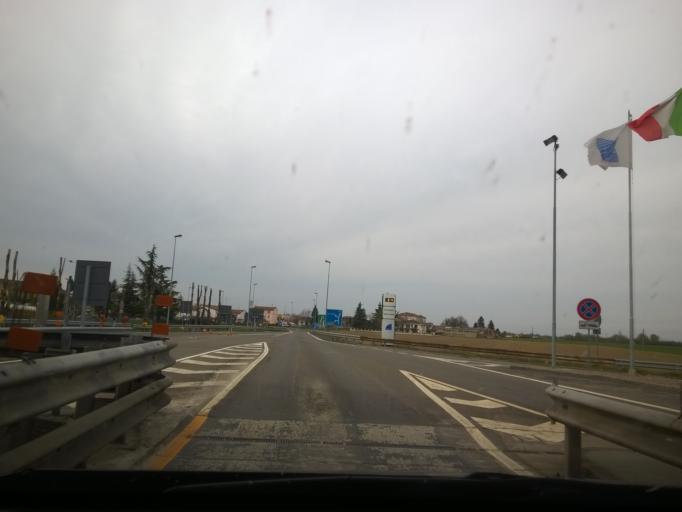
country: IT
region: Lombardy
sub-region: Provincia di Pavia
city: Casatisma
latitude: 45.0405
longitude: 9.1333
